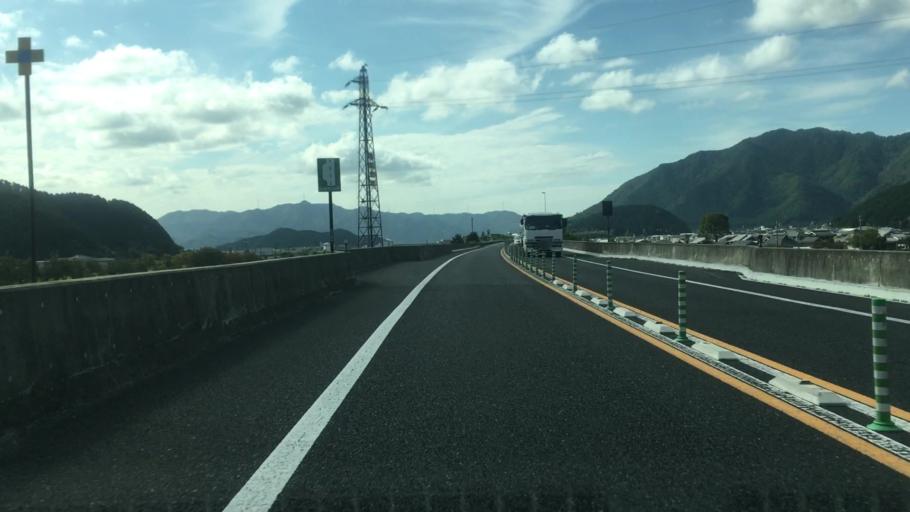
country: JP
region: Kyoto
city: Fukuchiyama
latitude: 35.1929
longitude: 135.0425
